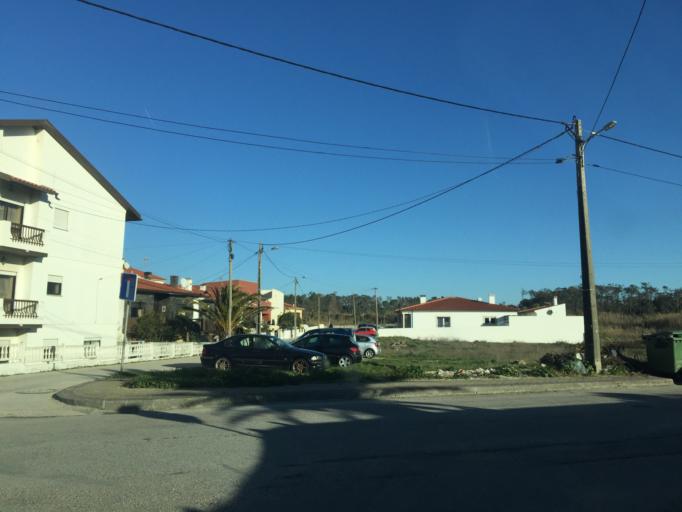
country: PT
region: Coimbra
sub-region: Figueira da Foz
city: Lavos
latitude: 40.0898
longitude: -8.8737
